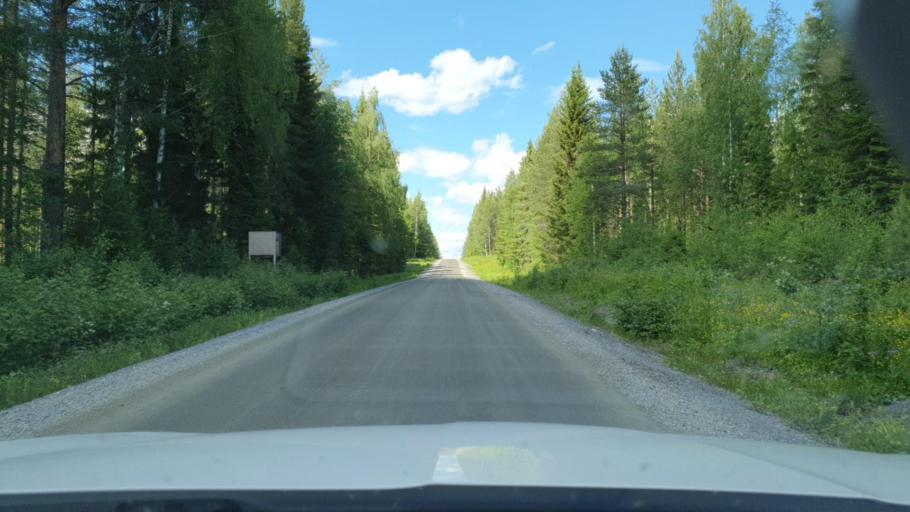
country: SE
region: Vaesterbotten
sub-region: Skelleftea Kommun
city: Forsbacka
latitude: 64.7956
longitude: 20.5062
